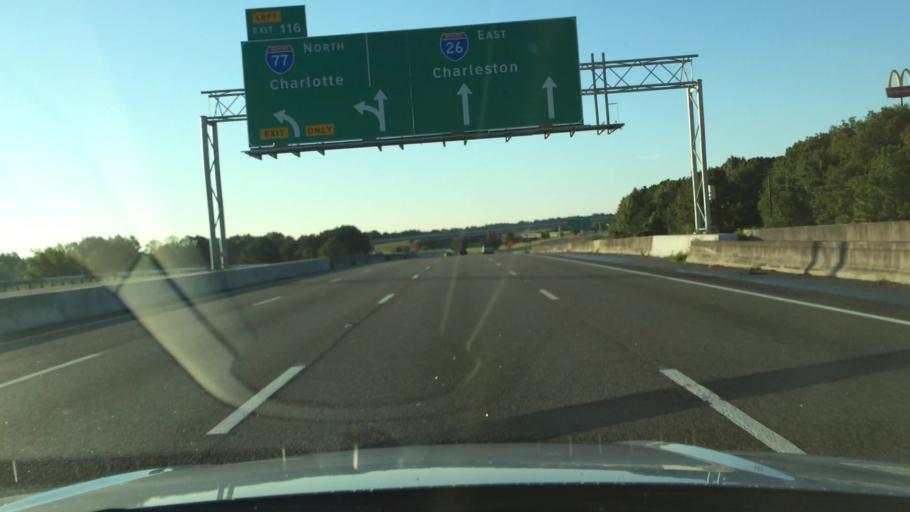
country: US
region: South Carolina
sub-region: Lexington County
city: Cayce
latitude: 33.9327
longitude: -81.0766
